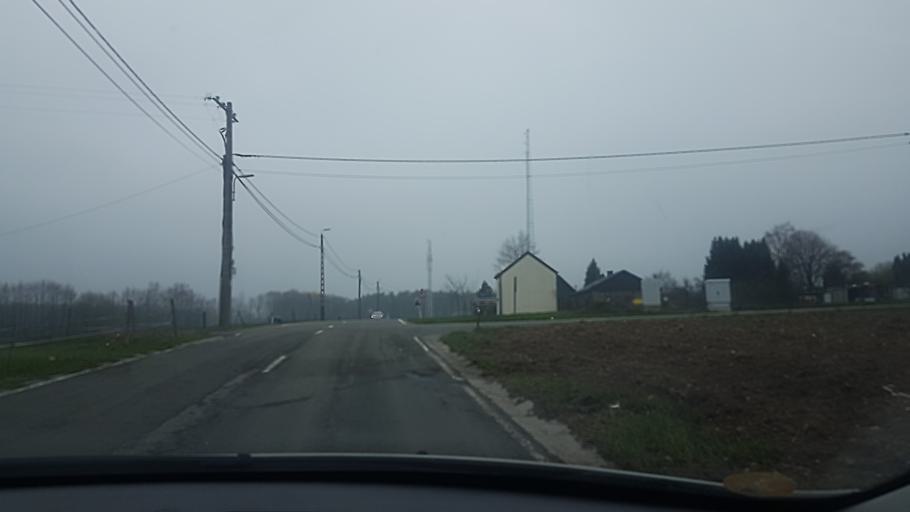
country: FR
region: Champagne-Ardenne
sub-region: Departement des Ardennes
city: Haybes
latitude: 50.0256
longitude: 4.6326
